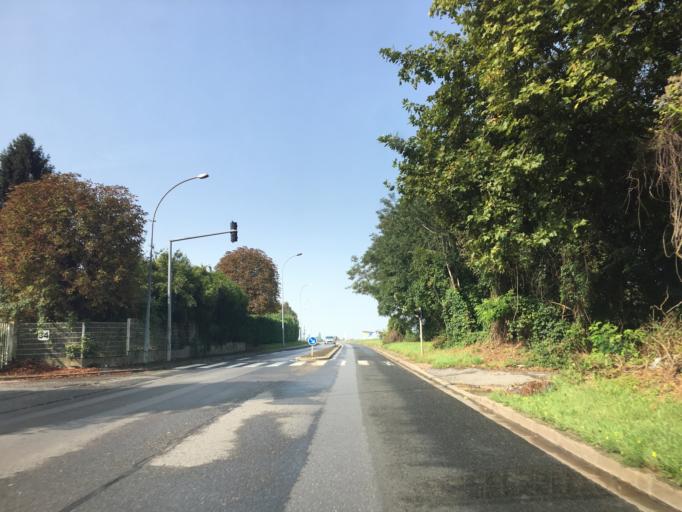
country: FR
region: Ile-de-France
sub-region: Departement du Val-de-Marne
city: Noiseau
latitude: 48.7810
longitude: 2.5624
